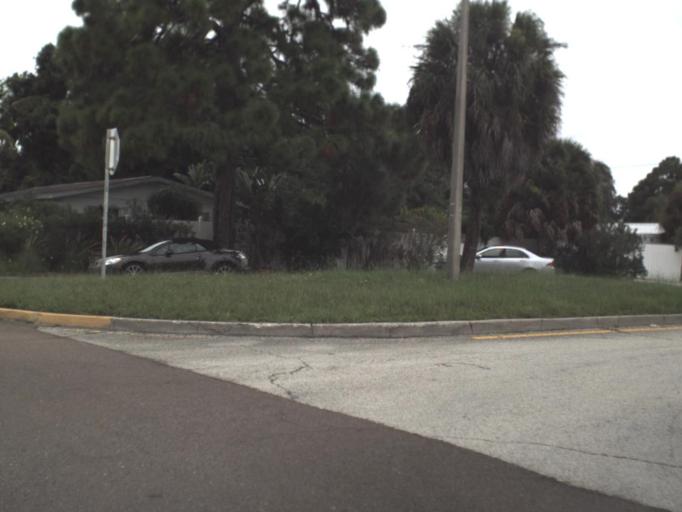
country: US
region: Florida
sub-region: Sarasota County
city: Sarasota Springs
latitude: 27.2989
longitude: -82.4675
